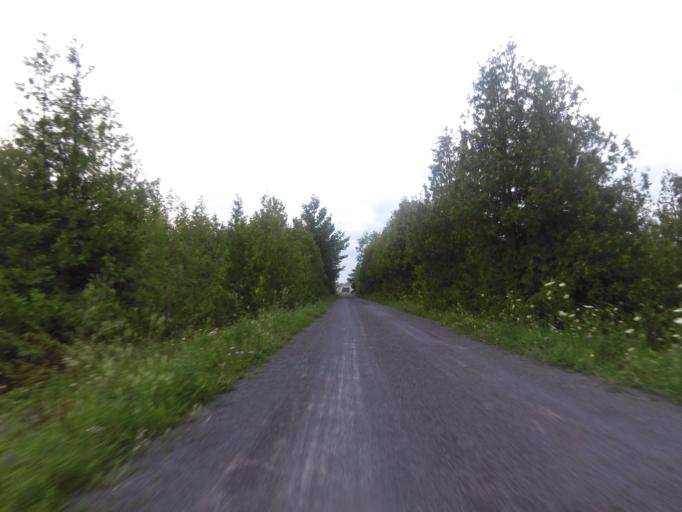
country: CA
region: Ontario
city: Carleton Place
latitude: 45.1801
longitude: -76.0444
